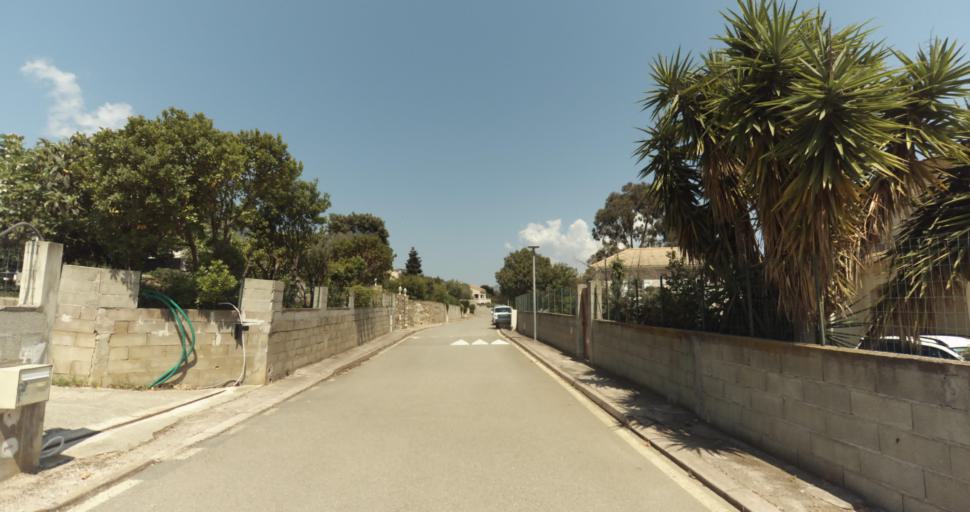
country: FR
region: Corsica
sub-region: Departement de la Haute-Corse
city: Biguglia
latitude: 42.6038
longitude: 9.4338
